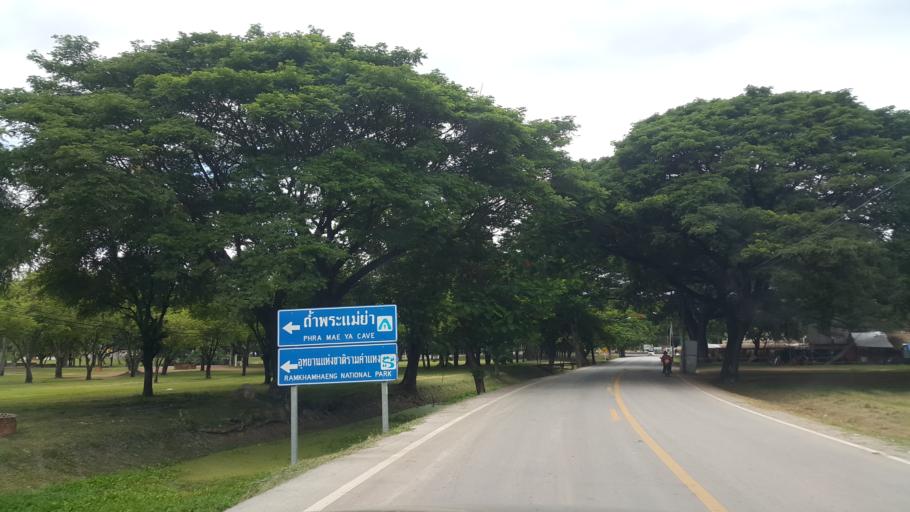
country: TH
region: Sukhothai
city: Ban Na
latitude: 17.0233
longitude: 99.7038
